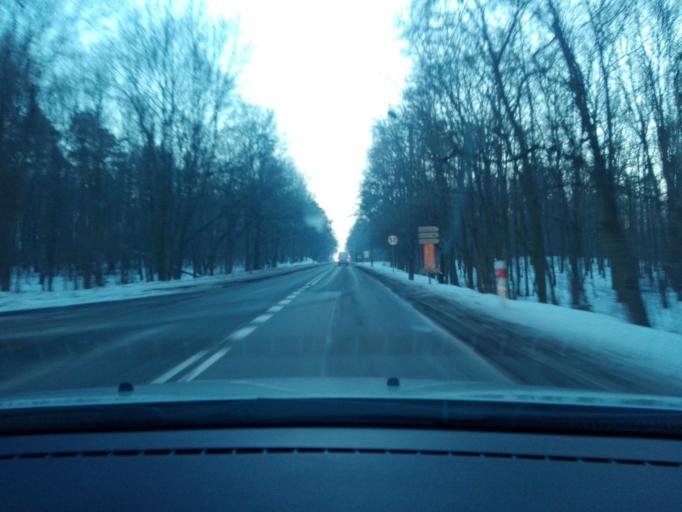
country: PL
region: Lodz Voivodeship
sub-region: Powiat zgierski
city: Zgierz
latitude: 51.8809
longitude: 19.4132
